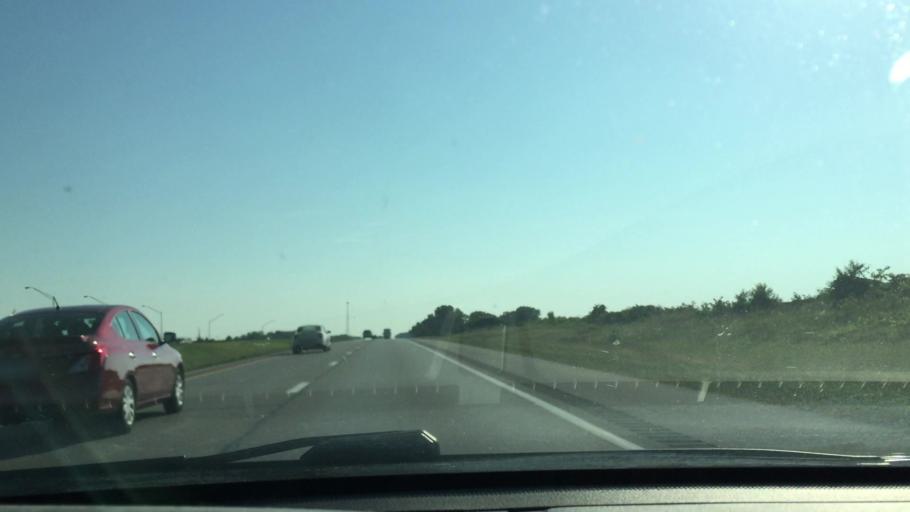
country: US
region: Ohio
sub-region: Clinton County
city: Wilmington
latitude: 39.5100
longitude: -83.8734
